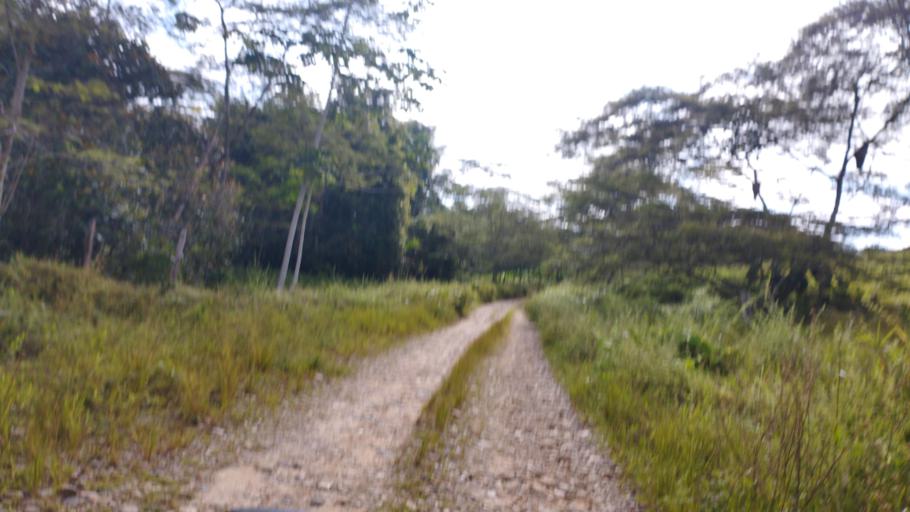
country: CO
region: Casanare
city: Sabanalarga
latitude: 4.7591
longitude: -73.0729
